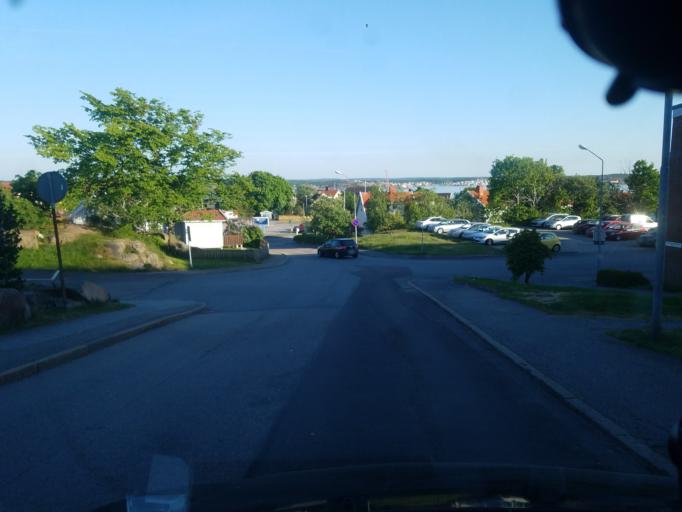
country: SE
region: Vaestra Goetaland
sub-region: Lysekils Kommun
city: Lysekil
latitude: 58.2804
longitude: 11.4548
